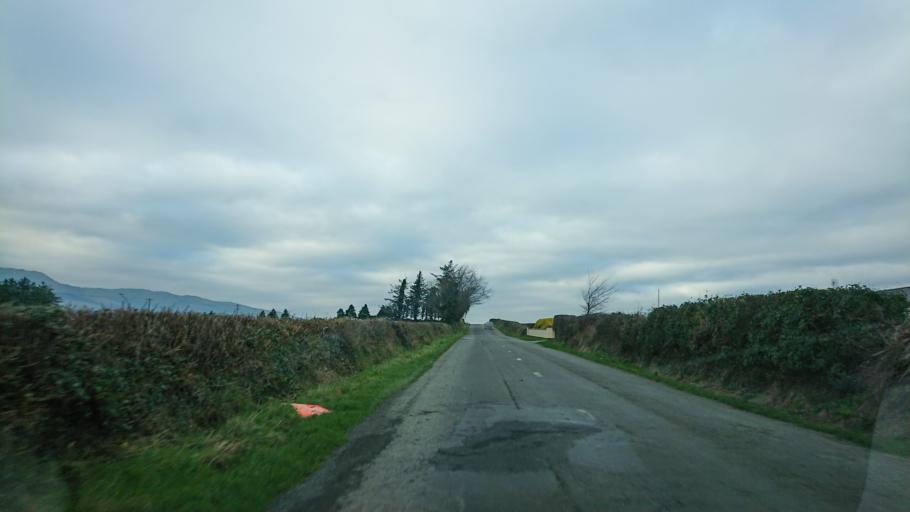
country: IE
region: Munster
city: Carrick-on-Suir
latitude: 52.3023
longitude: -7.4859
